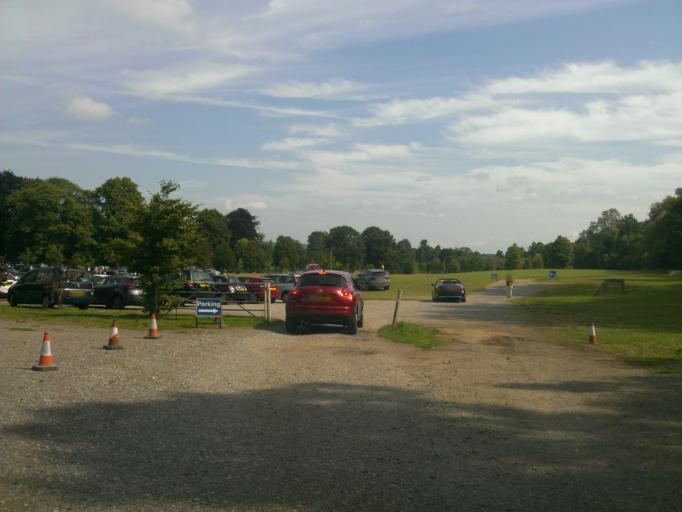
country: GB
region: England
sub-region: Kent
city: Edenbridge
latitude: 51.1845
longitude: 0.1194
